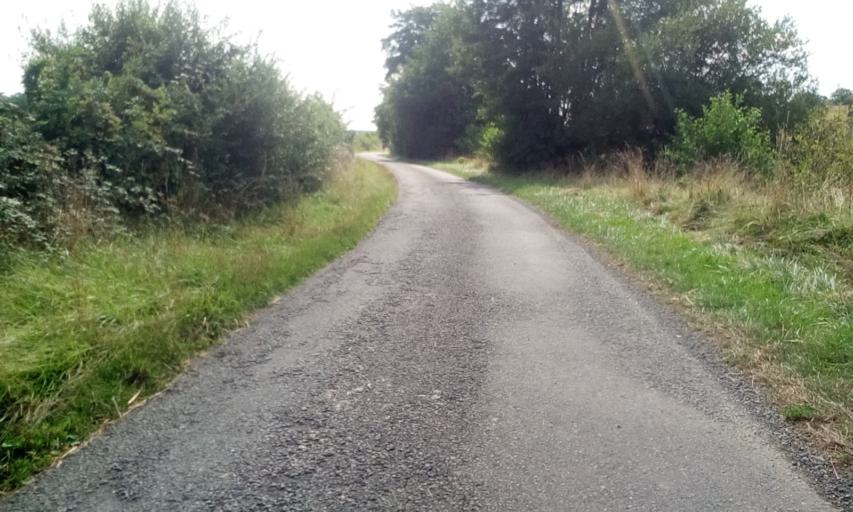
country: FR
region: Lower Normandy
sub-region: Departement du Calvados
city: Argences
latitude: 49.1566
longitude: -0.1554
